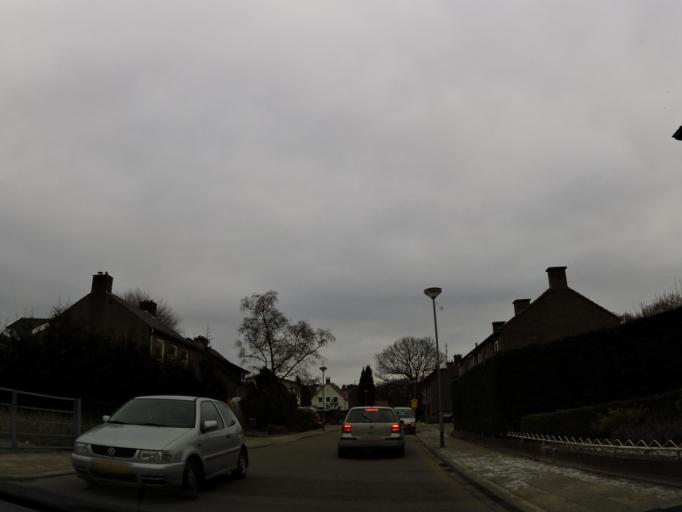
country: NL
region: Limburg
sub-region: Gemeente Onderbanken
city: Schinveld
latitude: 50.9636
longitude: 5.9861
